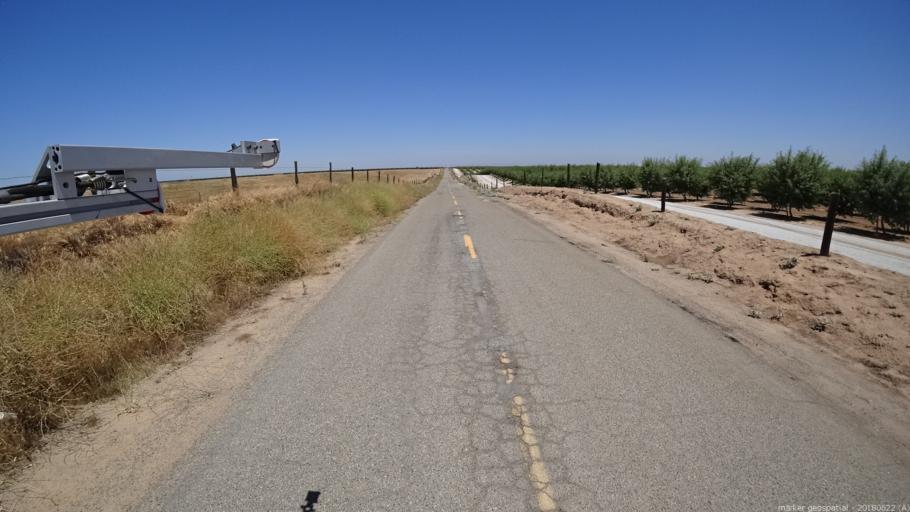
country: US
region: California
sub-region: Madera County
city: Bonadelle Ranchos-Madera Ranchos
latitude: 36.8665
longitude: -119.8390
